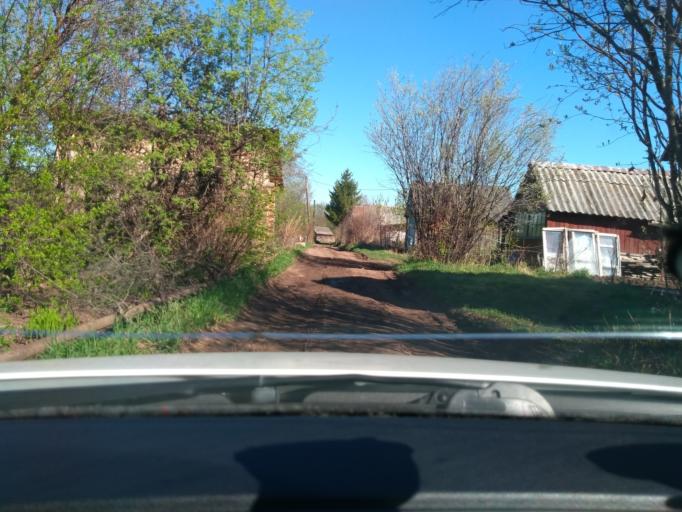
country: RU
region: Perm
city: Lobanovo
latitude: 57.8705
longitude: 56.3037
